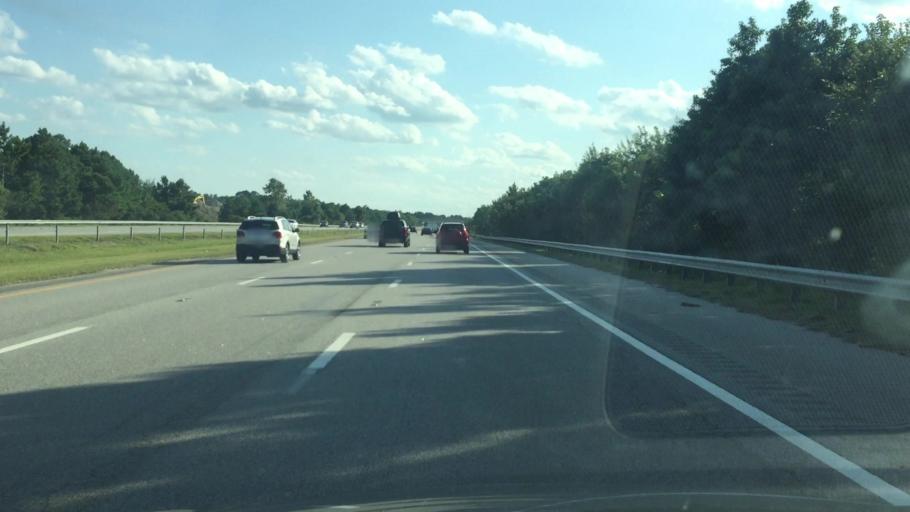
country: US
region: South Carolina
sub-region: Horry County
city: North Myrtle Beach
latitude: 33.8233
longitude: -78.7354
